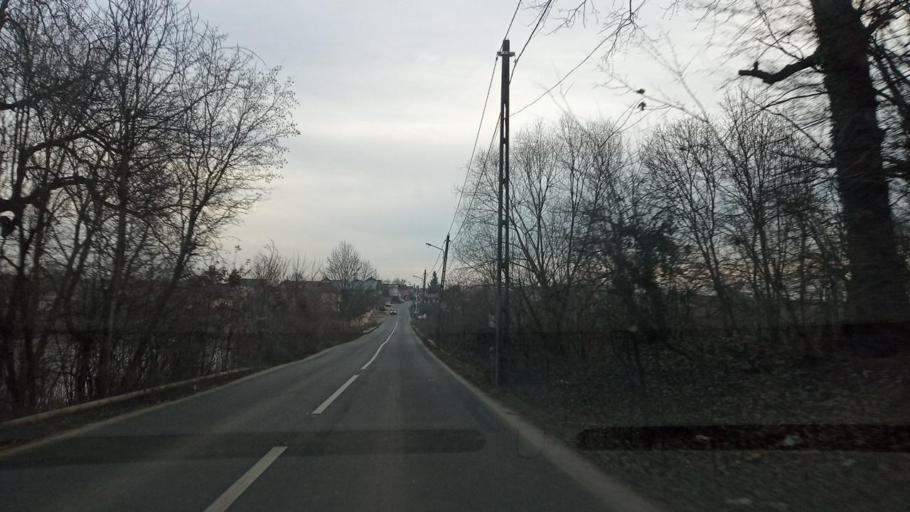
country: RO
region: Ilfov
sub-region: Comuna Ganeasa
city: Ganeasa
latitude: 44.4779
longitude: 26.2948
